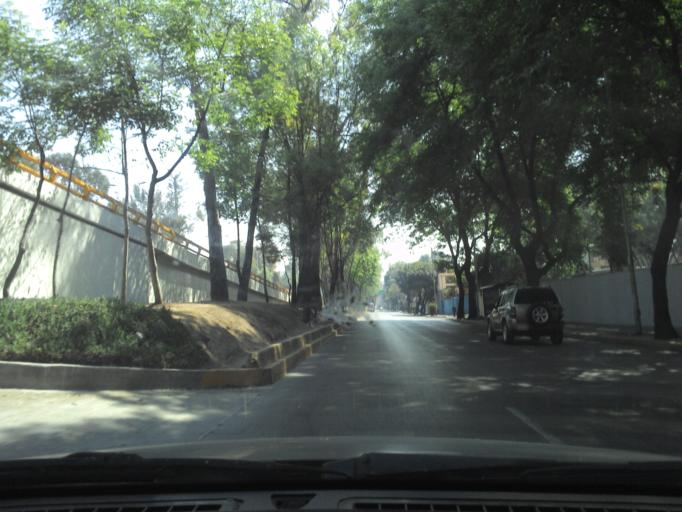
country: MX
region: Mexico City
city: Coyoacan
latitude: 19.3580
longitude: -99.1626
